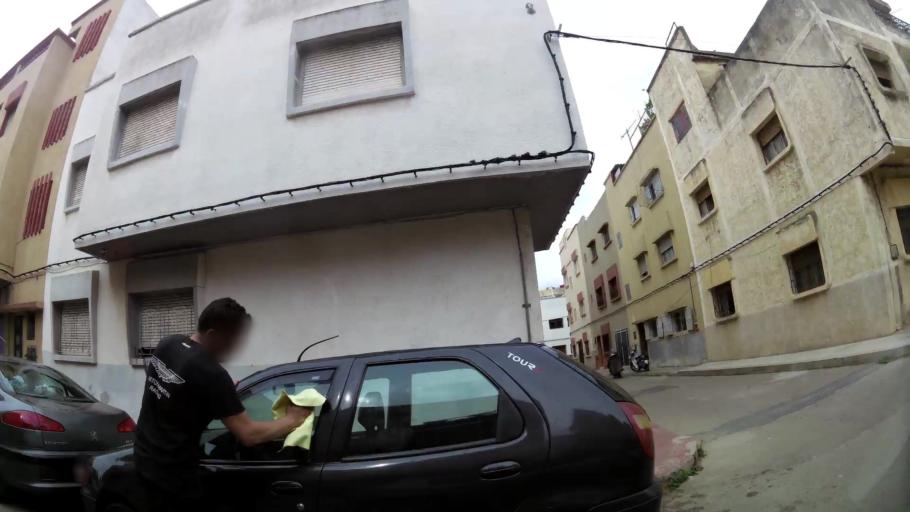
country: MA
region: Rabat-Sale-Zemmour-Zaer
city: Sale
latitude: 34.0292
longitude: -6.8023
